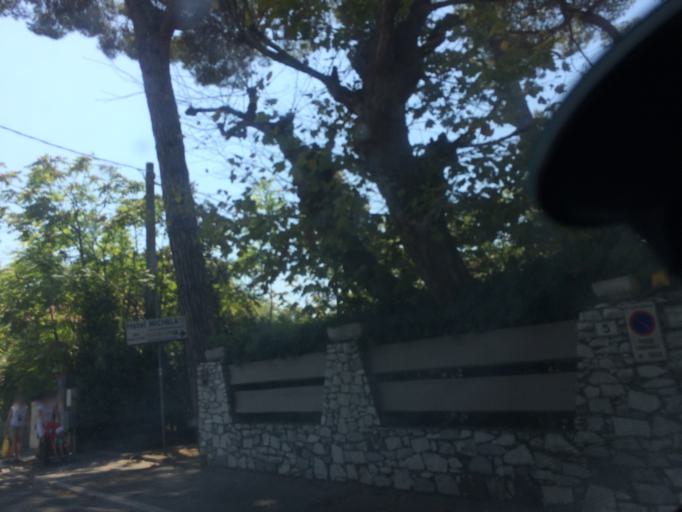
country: IT
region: Tuscany
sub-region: Provincia di Massa-Carrara
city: Massa
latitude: 44.0117
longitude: 10.0970
